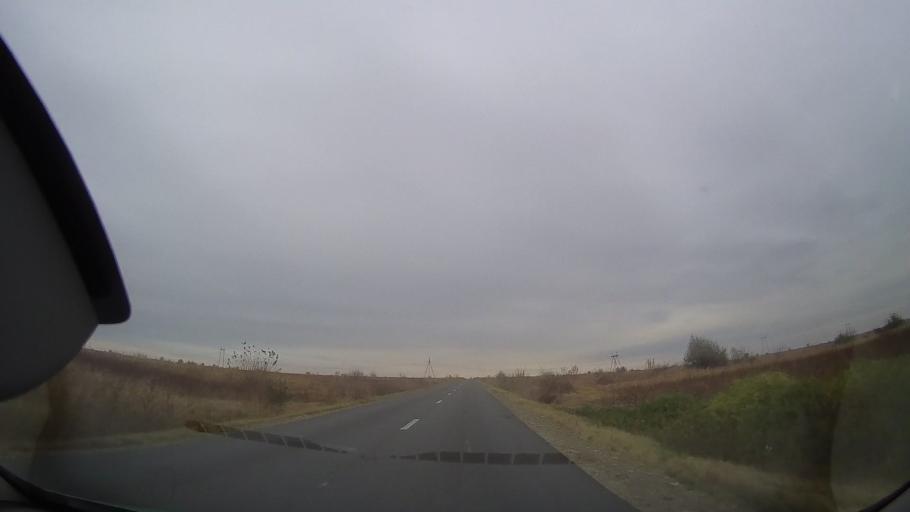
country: RO
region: Ialomita
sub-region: Oras Amara
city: Amara
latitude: 44.6346
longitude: 27.3009
